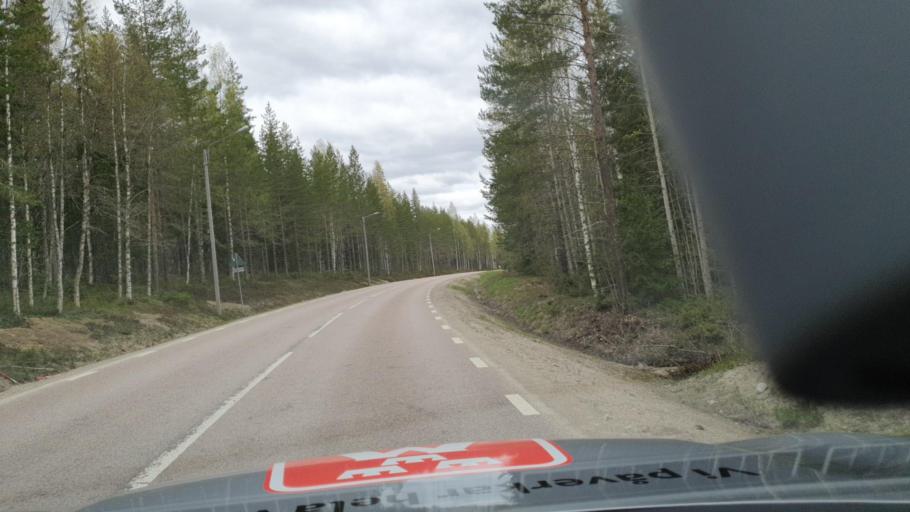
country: SE
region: Vaesternorrland
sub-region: OErnskoeldsviks Kommun
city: Ornskoldsvik
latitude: 63.4887
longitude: 18.8778
